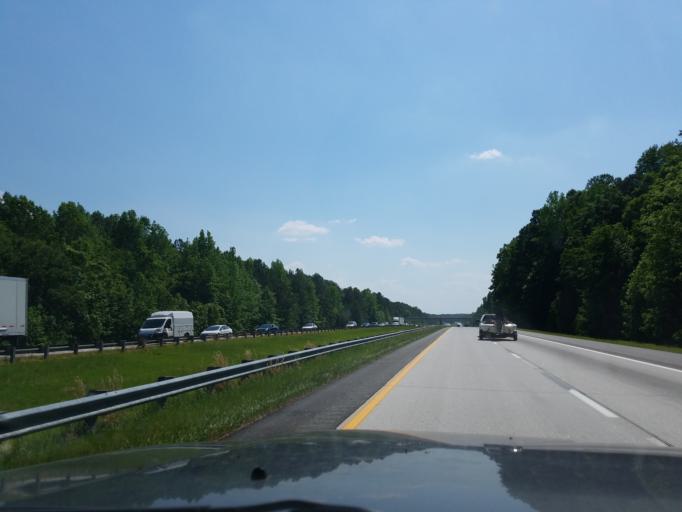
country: US
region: North Carolina
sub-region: Granville County
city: Creedmoor
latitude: 36.2213
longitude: -78.6599
